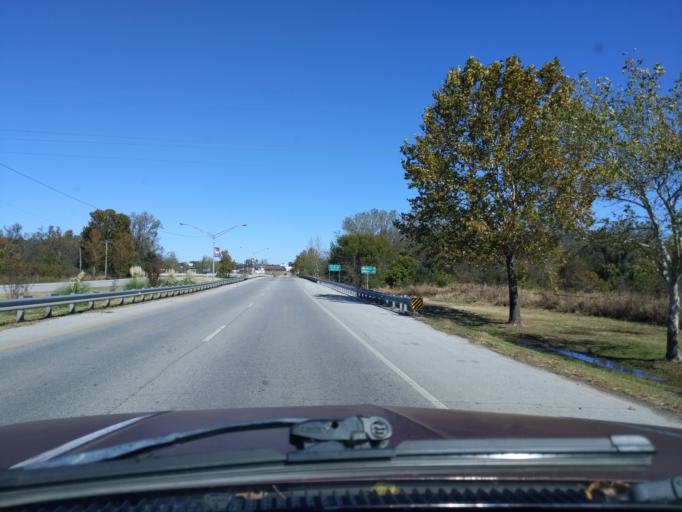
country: US
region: Oklahoma
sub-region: Creek County
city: Bristow
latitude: 35.8419
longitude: -96.3899
